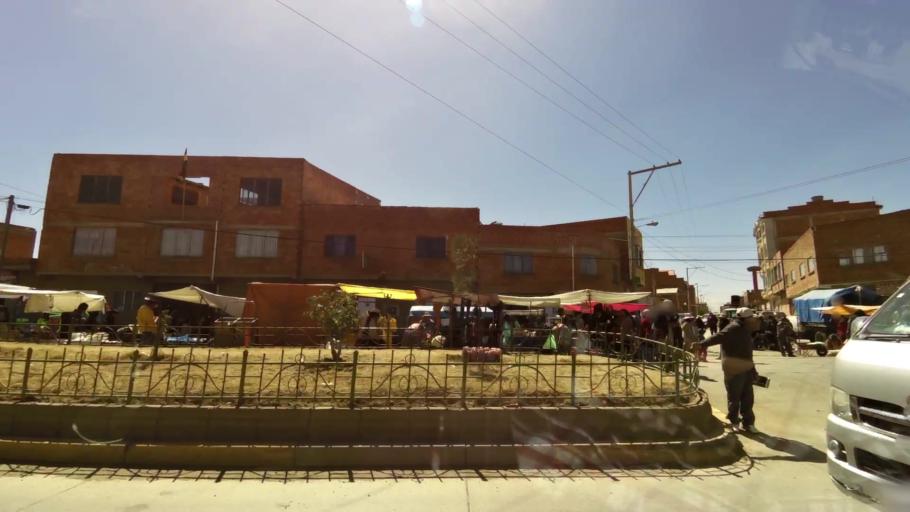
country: BO
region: La Paz
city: La Paz
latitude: -16.5005
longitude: -68.2265
